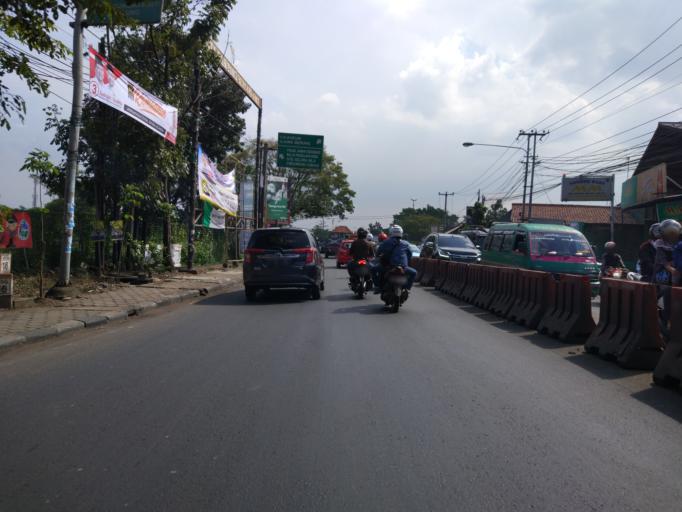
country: ID
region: West Java
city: Cileunyi
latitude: -6.9348
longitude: 107.7196
